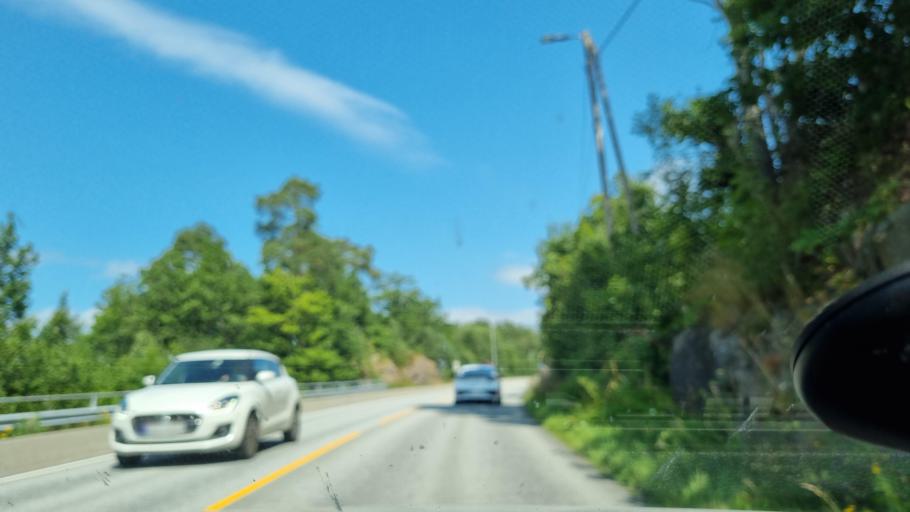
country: NO
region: Aust-Agder
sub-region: Arendal
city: Arendal
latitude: 58.4628
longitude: 8.8197
